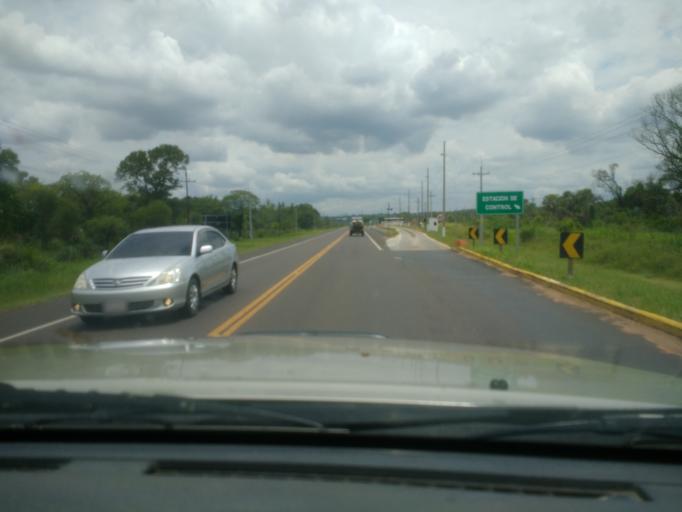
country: PY
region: Central
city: Limpio
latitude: -25.1208
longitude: -57.4332
